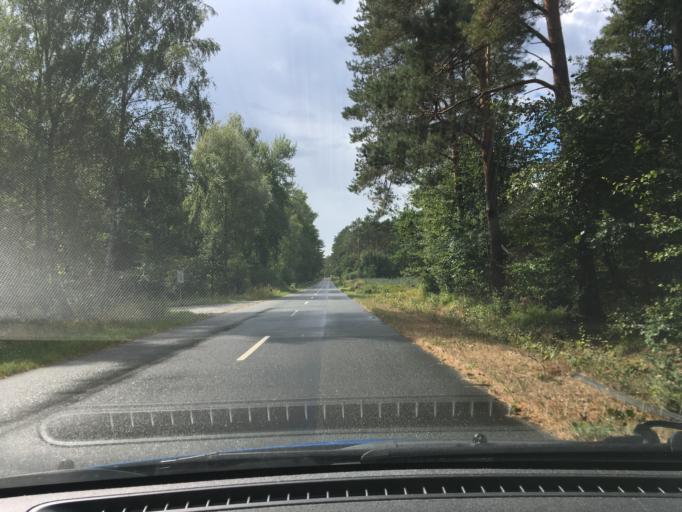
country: DE
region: Lower Saxony
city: Wietzendorf
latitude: 52.9849
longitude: 9.9767
